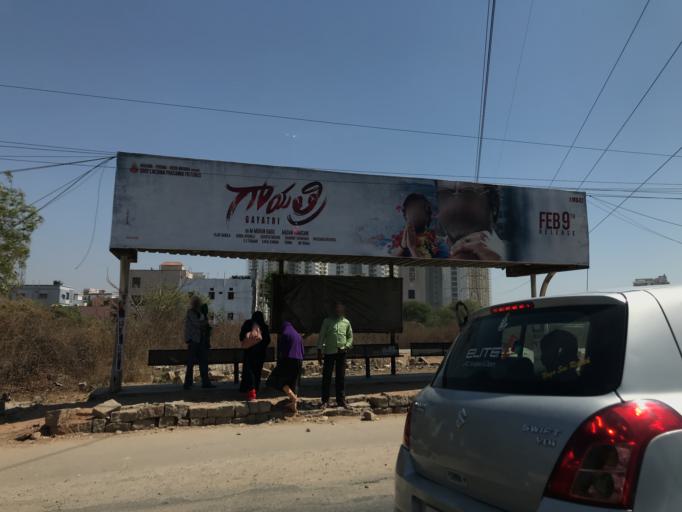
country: IN
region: Telangana
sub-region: Medak
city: Serilingampalle
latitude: 17.4689
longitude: 78.3307
